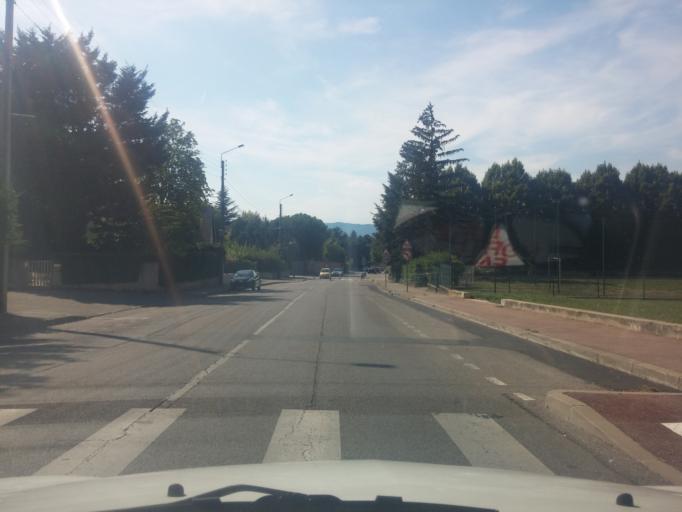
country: FR
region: Rhone-Alpes
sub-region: Departement du Rhone
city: Sainte-Foy-les-Lyon
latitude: 45.7356
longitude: 4.7980
